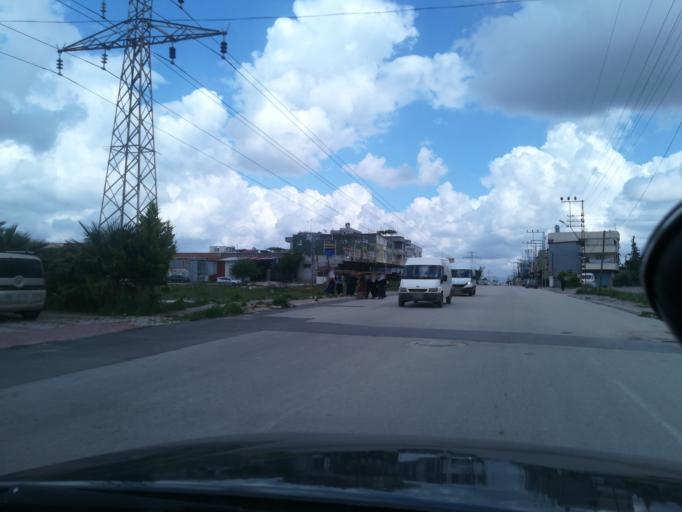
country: TR
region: Adana
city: Yuregir
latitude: 36.9756
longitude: 35.3912
